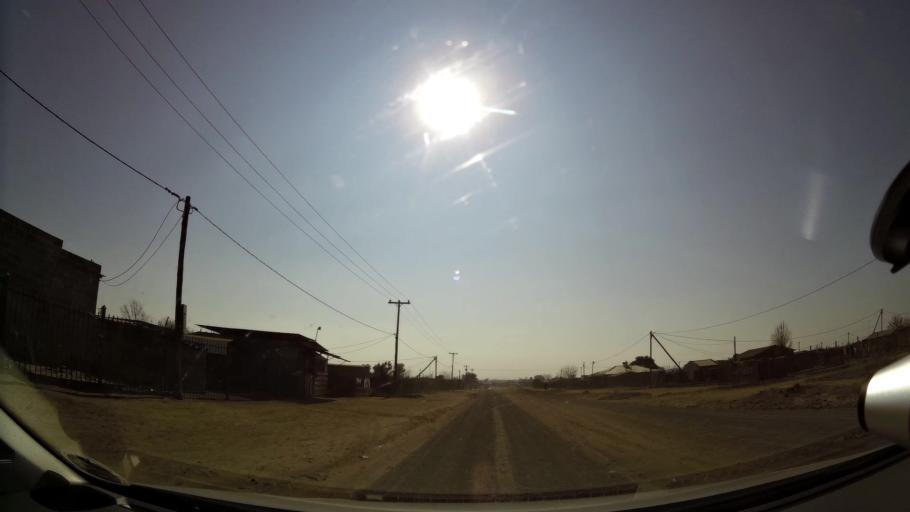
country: ZA
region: Orange Free State
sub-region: Mangaung Metropolitan Municipality
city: Bloemfontein
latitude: -29.1777
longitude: 26.2887
